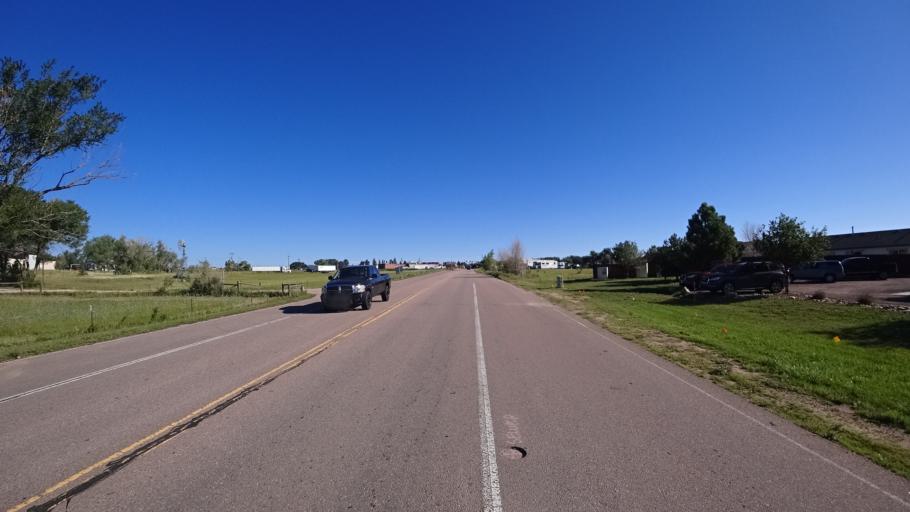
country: US
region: Colorado
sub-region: El Paso County
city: Cimarron Hills
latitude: 38.9305
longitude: -104.6083
